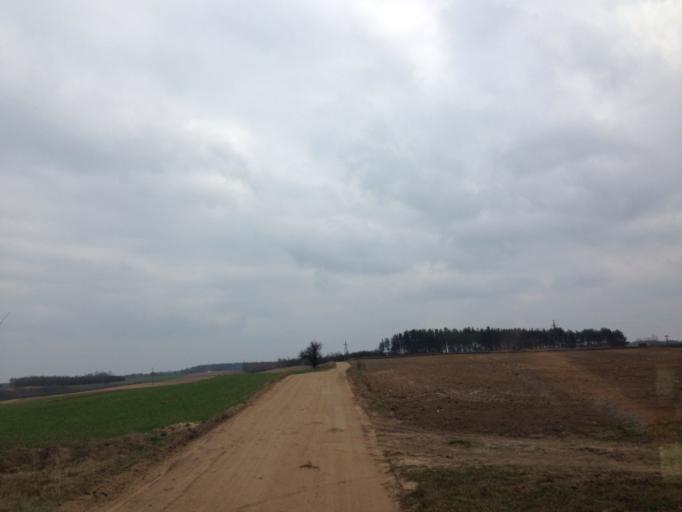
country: PL
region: Warmian-Masurian Voivodeship
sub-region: Powiat dzialdowski
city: Lidzbark
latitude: 53.3672
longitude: 19.7628
